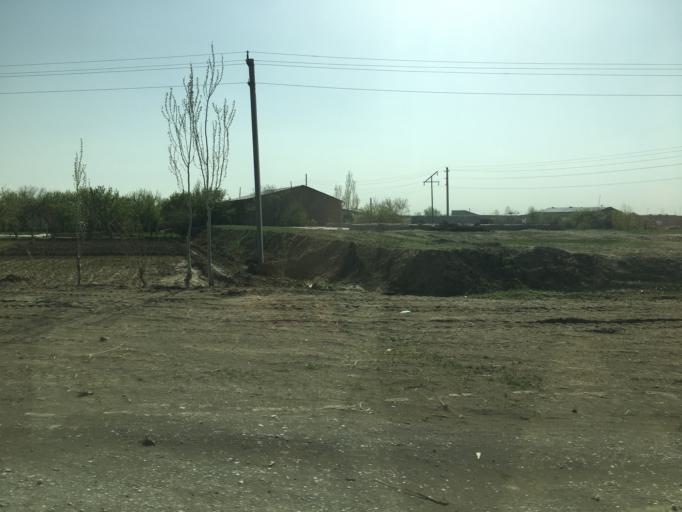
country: TM
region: Lebap
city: Farap
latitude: 39.2932
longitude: 63.4126
